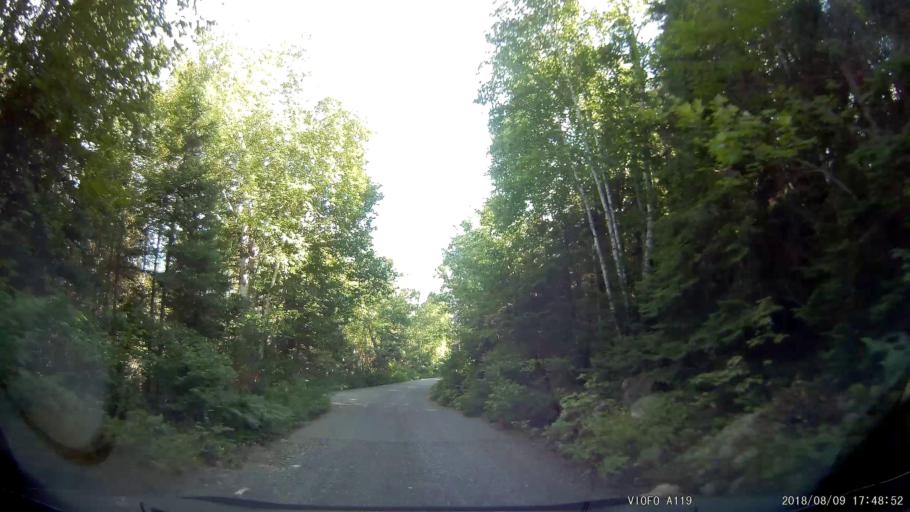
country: CA
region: Ontario
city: Rayside-Balfour
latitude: 46.5884
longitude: -81.5407
